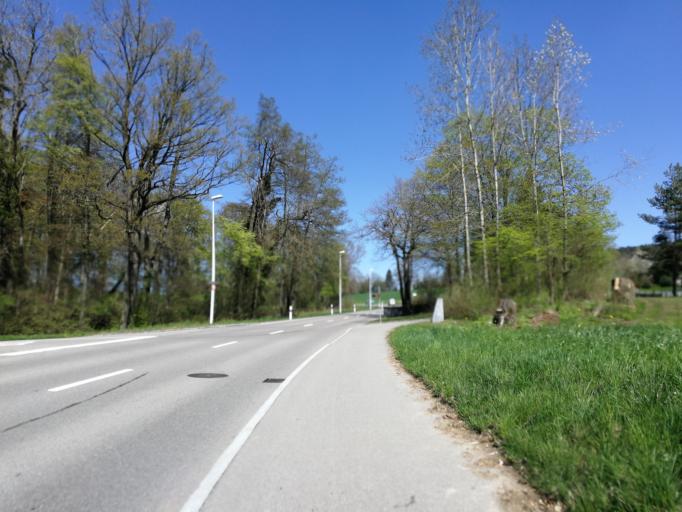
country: CH
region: Zurich
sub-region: Bezirk Meilen
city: Herrliberg
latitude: 47.2999
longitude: 8.6342
